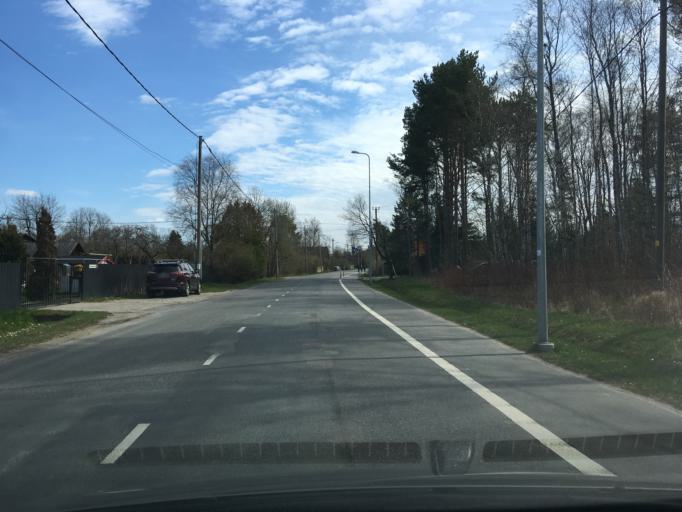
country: EE
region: Harju
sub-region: Joelaehtme vald
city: Loo
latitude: 59.4771
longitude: 24.9494
